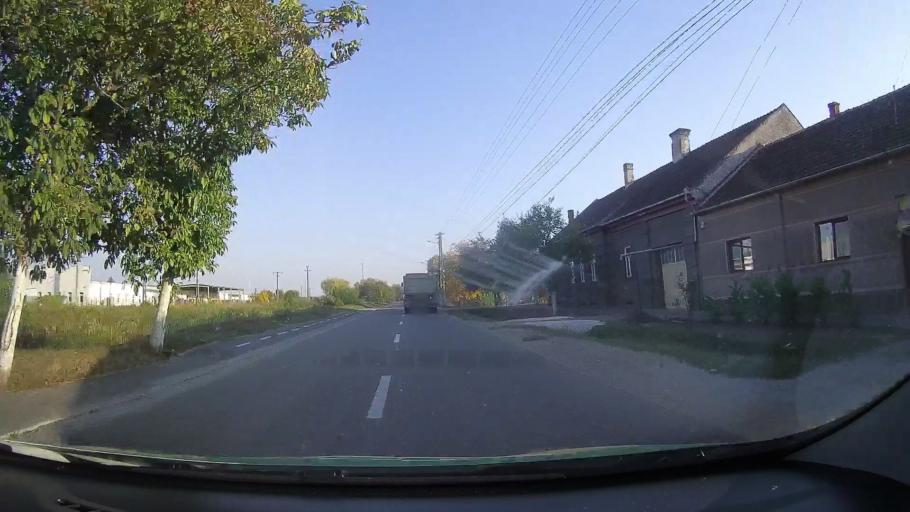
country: RO
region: Arad
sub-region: Comuna Pancota
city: Pancota
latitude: 46.3211
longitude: 21.6919
